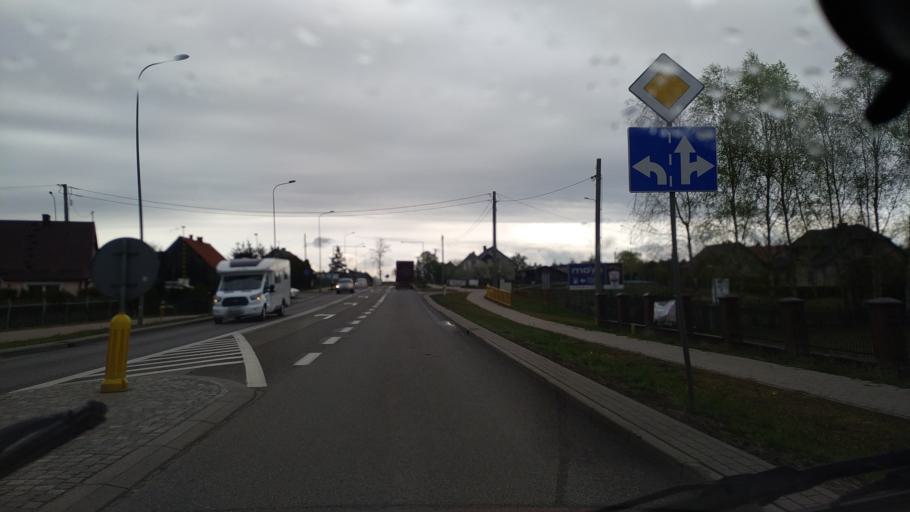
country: PL
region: Pomeranian Voivodeship
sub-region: Powiat starogardzki
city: Kaliska
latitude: 53.8979
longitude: 18.2366
